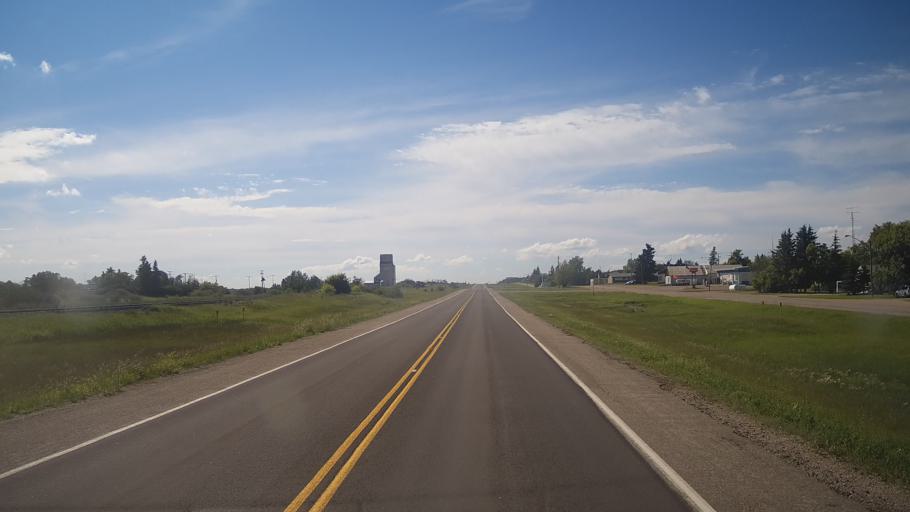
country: CA
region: Saskatchewan
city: Foam Lake
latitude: 51.2611
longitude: -103.7341
